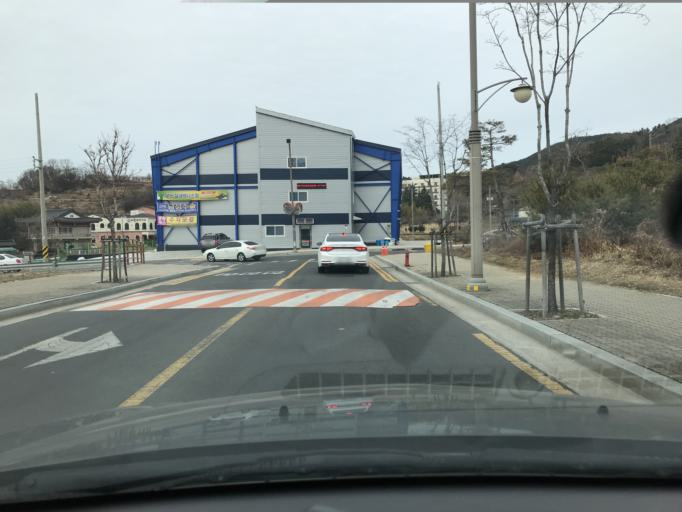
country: KR
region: Daegu
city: Hwawon
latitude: 35.6997
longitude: 128.4528
